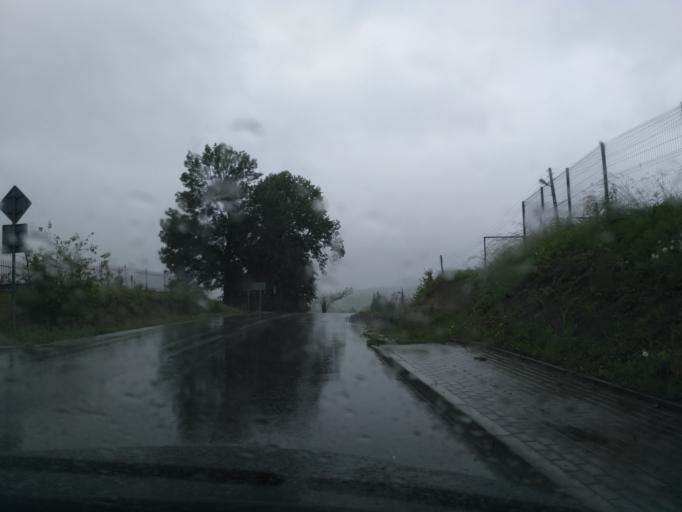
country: PL
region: Subcarpathian Voivodeship
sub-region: Powiat jasielski
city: Debowiec
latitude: 49.6771
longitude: 21.4583
